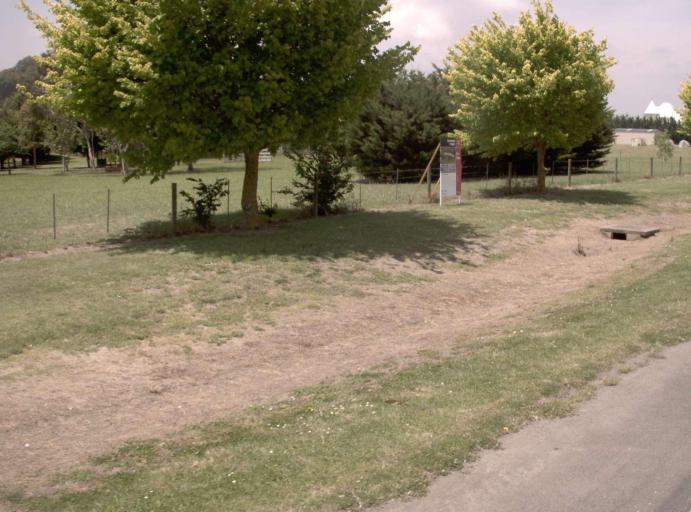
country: AU
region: Victoria
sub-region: Latrobe
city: Traralgon
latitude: -38.2050
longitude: 146.5442
